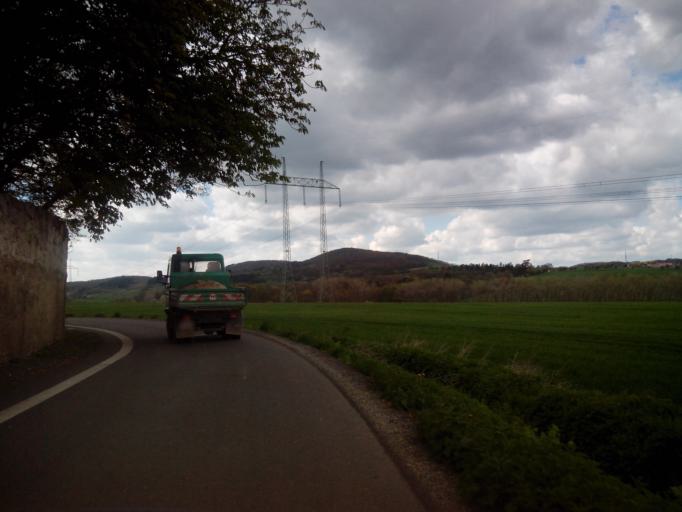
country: CZ
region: Central Bohemia
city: Revnice
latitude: 49.9071
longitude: 14.1498
